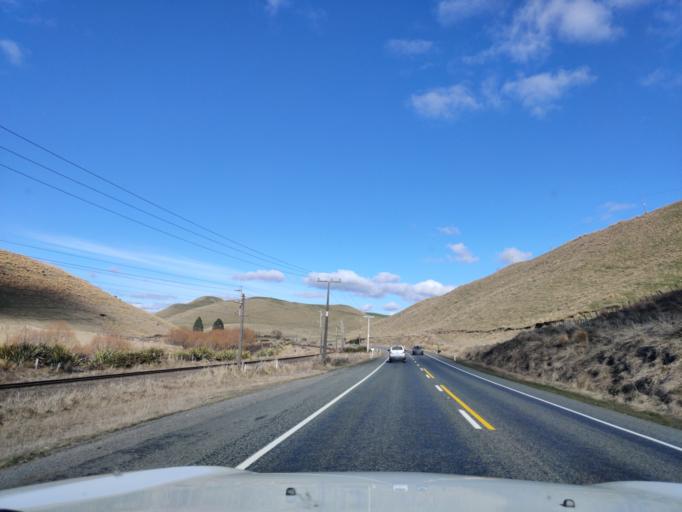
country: NZ
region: Manawatu-Wanganui
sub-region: Ruapehu District
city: Waiouru
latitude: -39.5028
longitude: 175.6739
